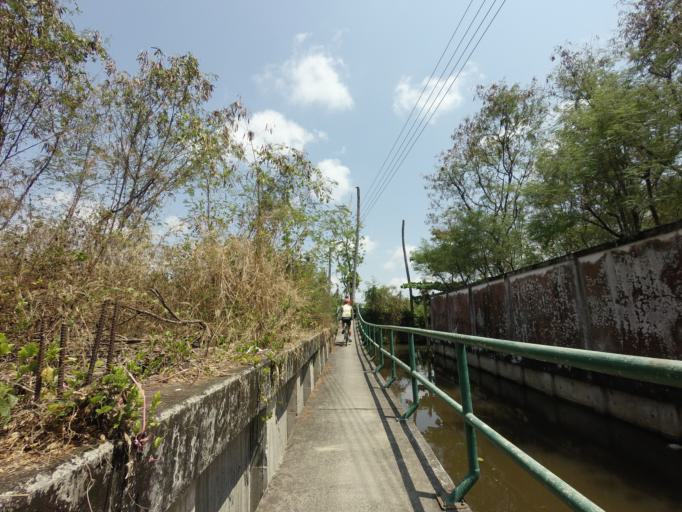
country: TH
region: Bangkok
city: Chom Thong
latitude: 13.6533
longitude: 100.4772
